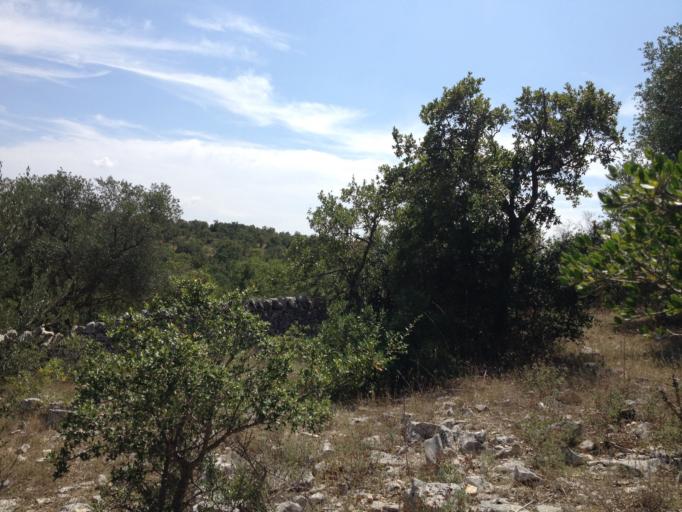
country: IT
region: Apulia
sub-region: Provincia di Bari
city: Gioia del Colle
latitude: 40.8284
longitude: 16.9922
